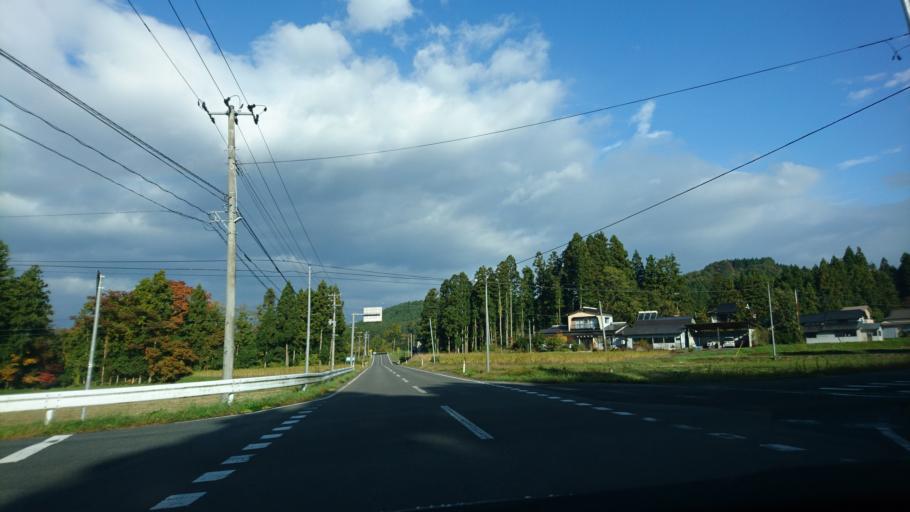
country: JP
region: Iwate
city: Mizusawa
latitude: 39.0534
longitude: 141.0445
